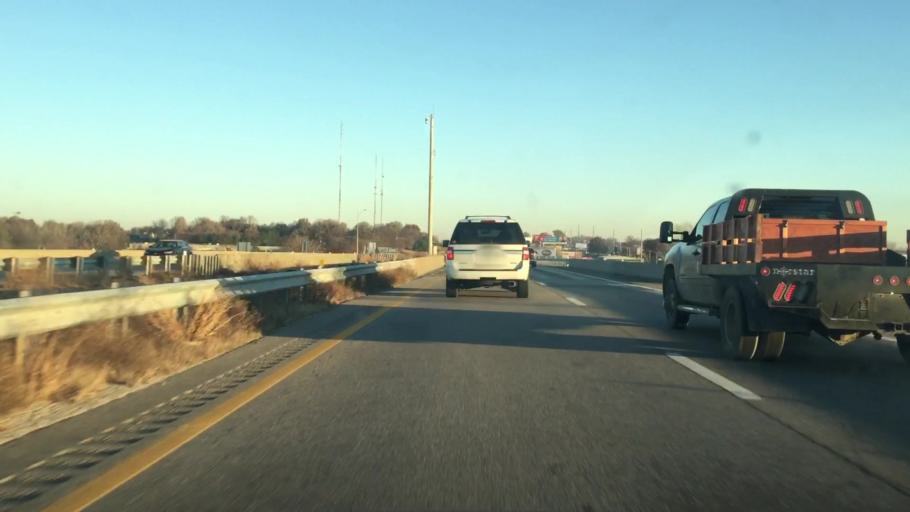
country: US
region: Missouri
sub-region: Buchanan County
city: Saint Joseph
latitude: 39.7238
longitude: -94.7884
